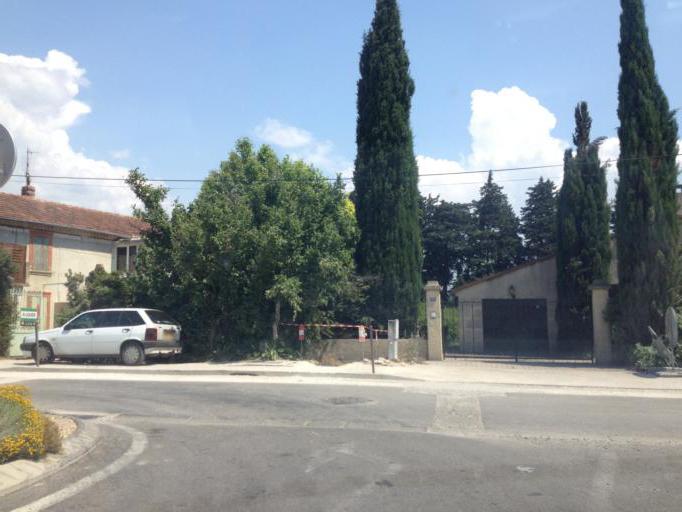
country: FR
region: Provence-Alpes-Cote d'Azur
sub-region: Departement du Vaucluse
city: Violes
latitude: 44.1639
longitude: 4.9531
